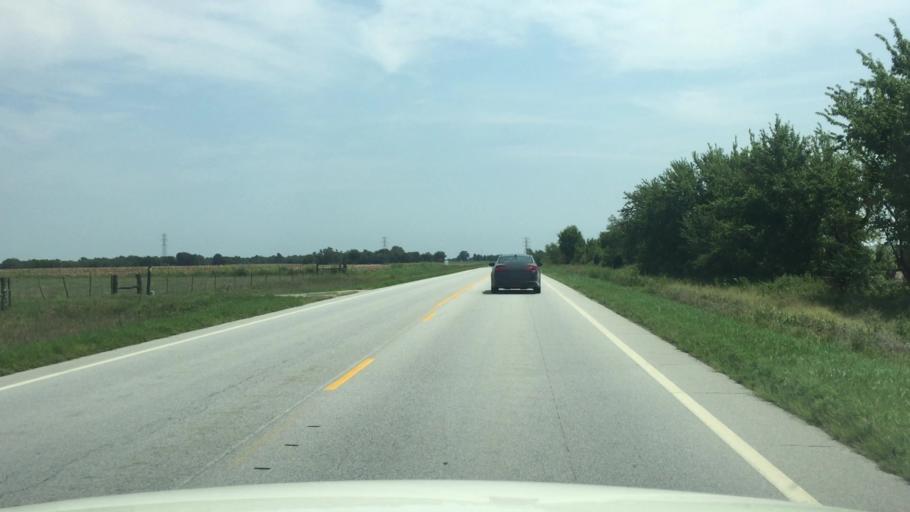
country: US
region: Kansas
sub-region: Cherokee County
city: Columbus
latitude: 37.1791
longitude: -94.9144
